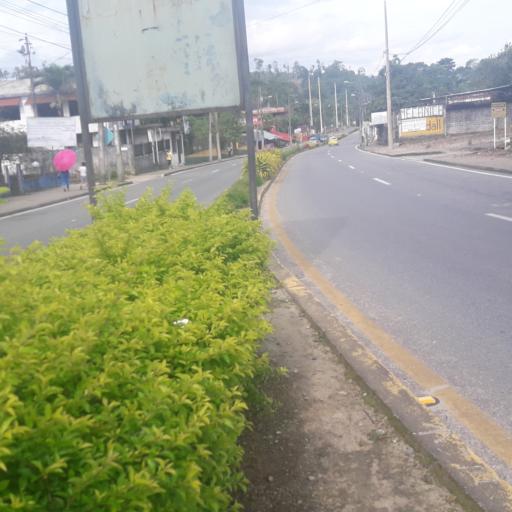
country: EC
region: Napo
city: Tena
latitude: -0.9834
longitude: -77.8121
